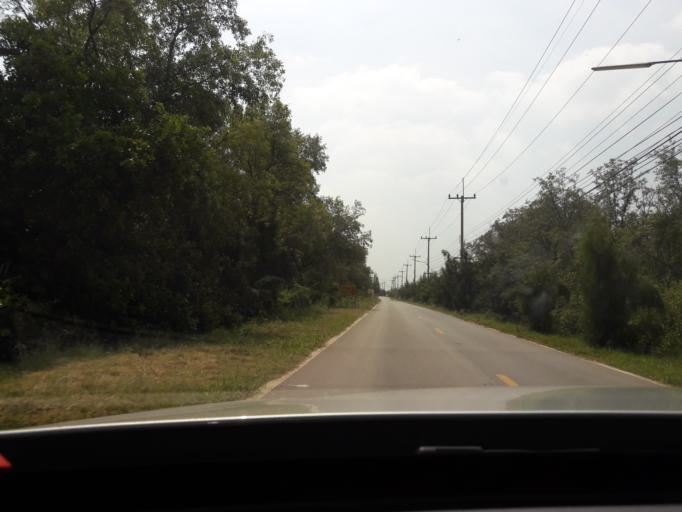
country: TH
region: Samut Songkhram
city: Amphawa
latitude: 13.3265
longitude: 99.9525
